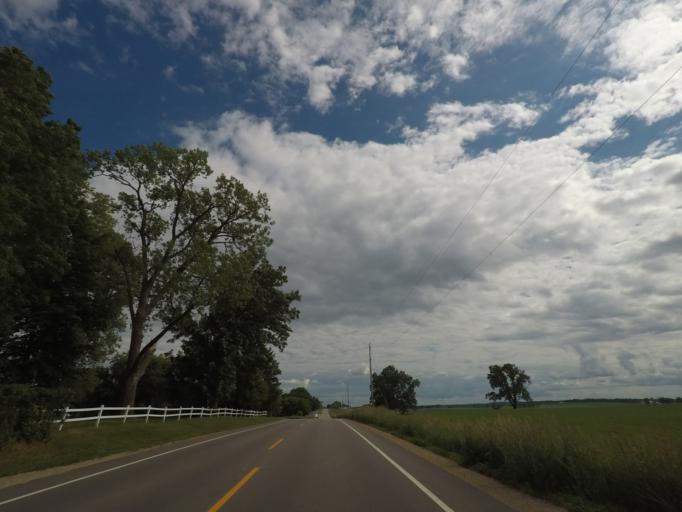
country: US
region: Wisconsin
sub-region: Green County
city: Albany
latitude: 42.7140
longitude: -89.3682
